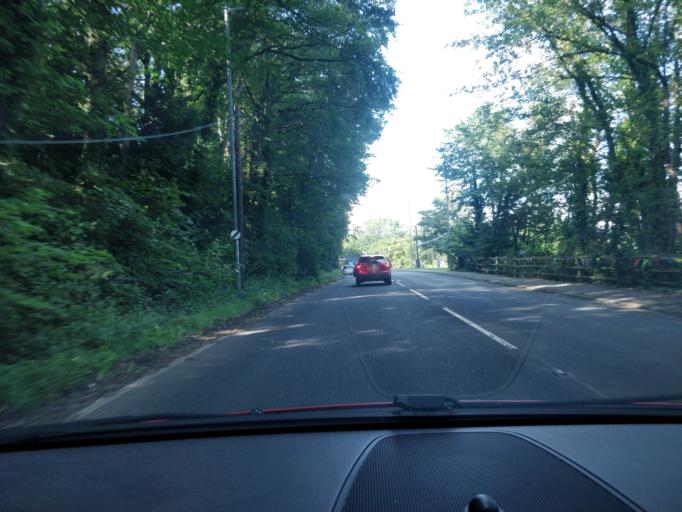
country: GB
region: Wales
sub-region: Conwy
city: Llansantffraid Glan Conwy
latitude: 53.2754
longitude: -3.7947
